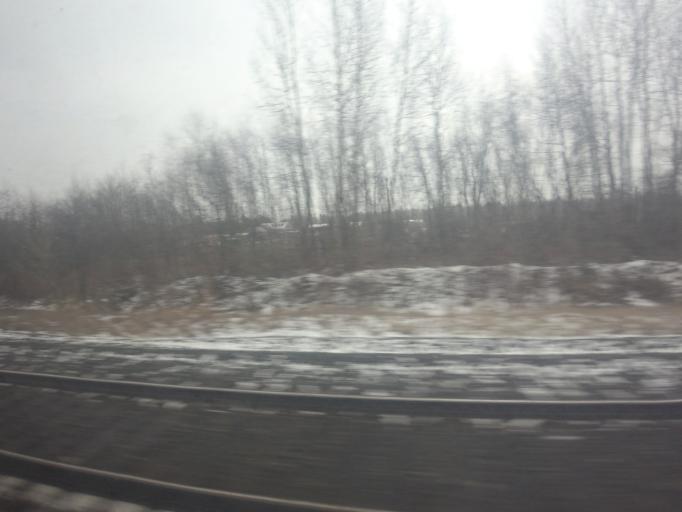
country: CA
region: Ontario
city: Quinte West
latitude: 44.0335
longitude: -77.7502
